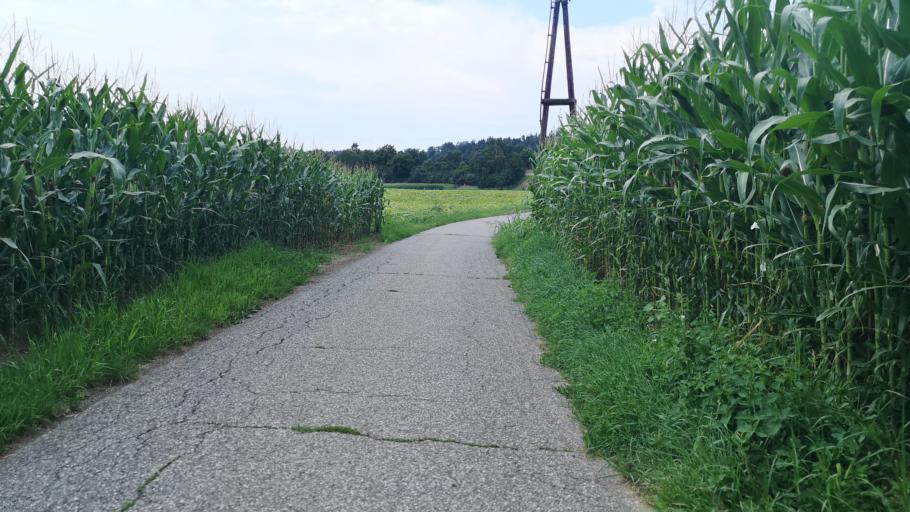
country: AT
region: Styria
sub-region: Politischer Bezirk Leibnitz
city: Weitendorf
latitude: 46.8891
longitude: 15.4752
